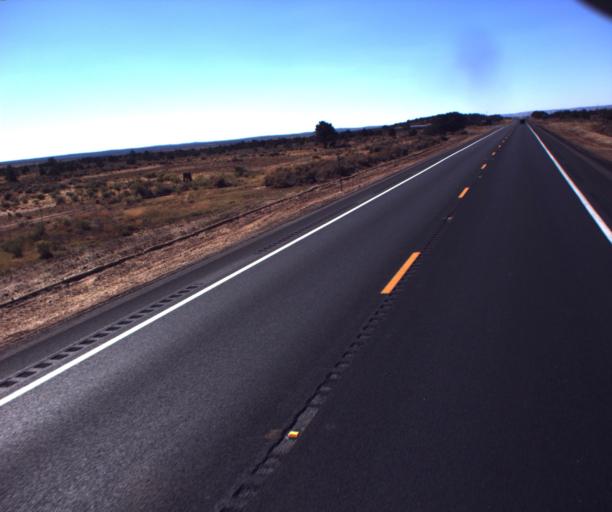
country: US
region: Arizona
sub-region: Apache County
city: Ganado
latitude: 35.7175
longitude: -109.4050
